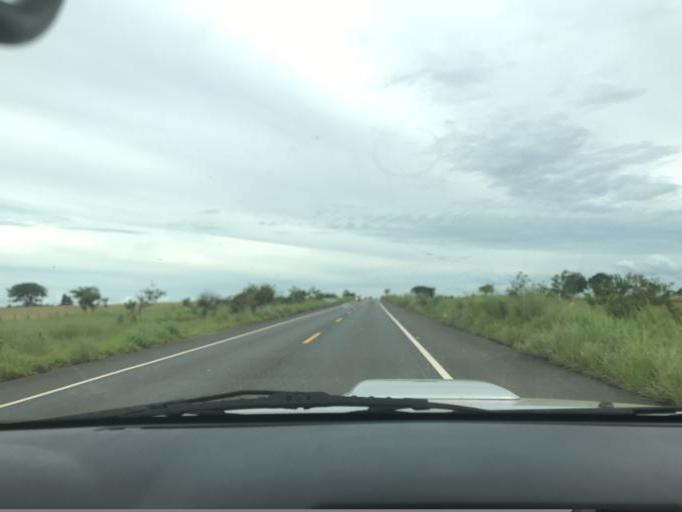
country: BR
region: Minas Gerais
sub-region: Araxa
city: Araxa
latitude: -19.3891
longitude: -46.8578
